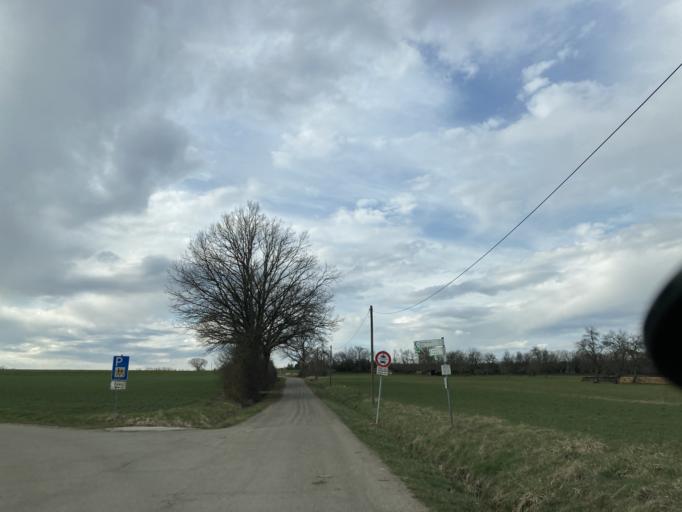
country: DE
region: Baden-Wuerttemberg
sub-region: Tuebingen Region
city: Dusslingen
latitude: 48.4588
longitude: 9.0486
